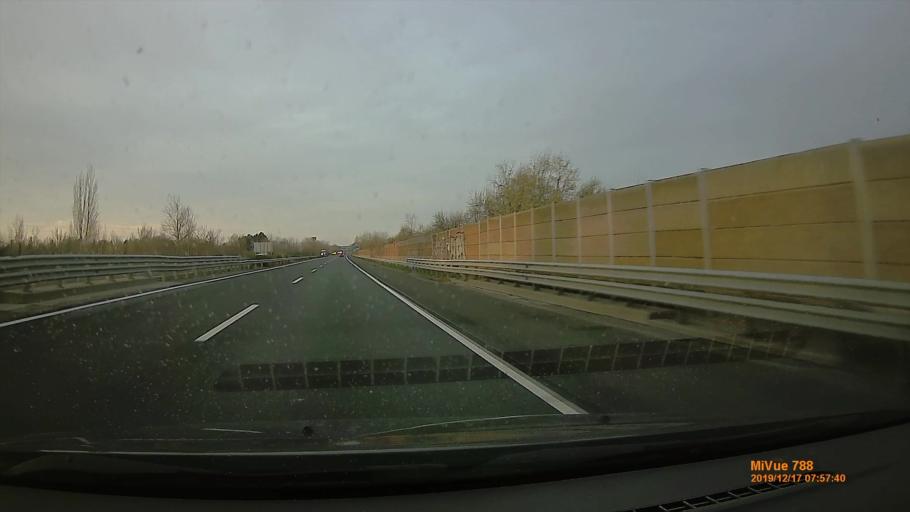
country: HU
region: Somogy
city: Siofok
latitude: 46.8999
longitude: 18.0679
